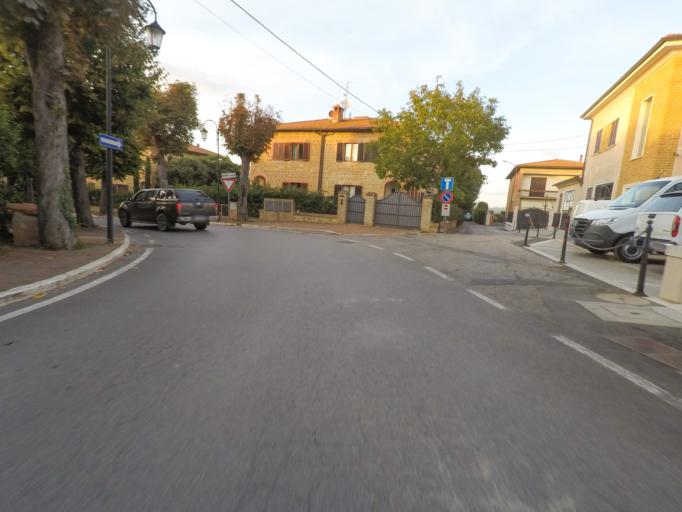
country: IT
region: Tuscany
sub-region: Provincia di Siena
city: Pienza
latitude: 43.0777
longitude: 11.6788
